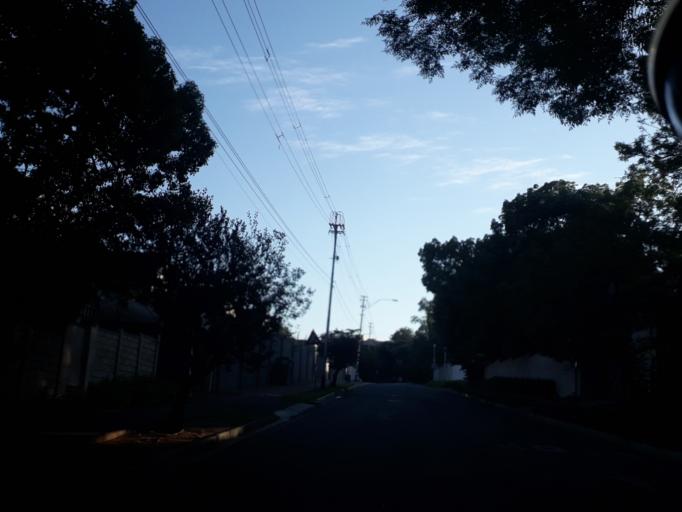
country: ZA
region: Gauteng
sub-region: City of Johannesburg Metropolitan Municipality
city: Johannesburg
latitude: -26.1133
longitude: 28.0280
